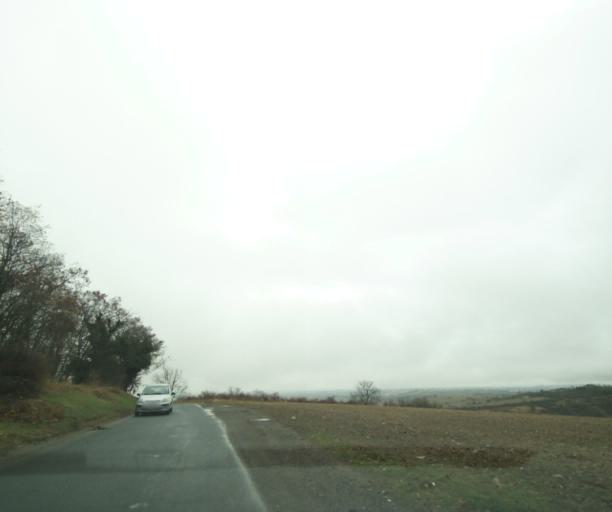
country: FR
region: Auvergne
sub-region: Departement du Puy-de-Dome
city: Cournon-d'Auvergne
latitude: 45.7569
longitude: 3.2040
